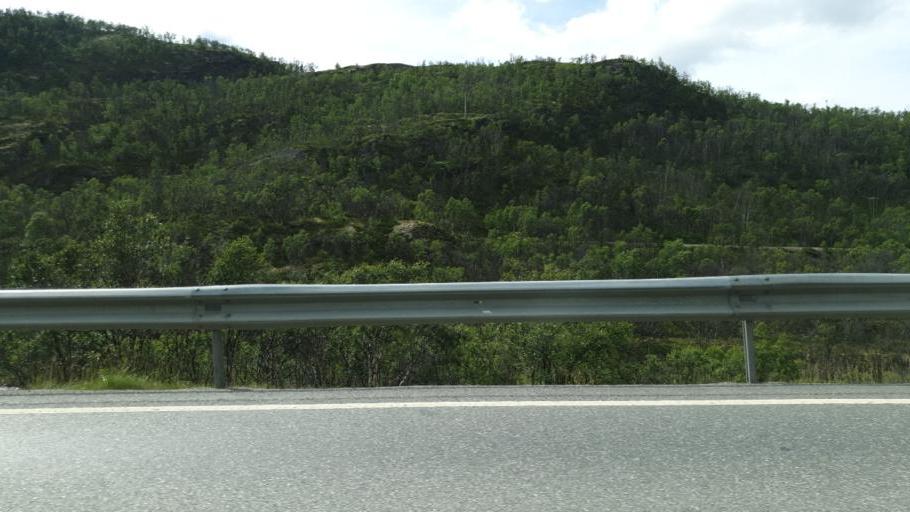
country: NO
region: Sor-Trondelag
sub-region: Oppdal
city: Oppdal
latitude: 62.2954
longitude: 9.5948
